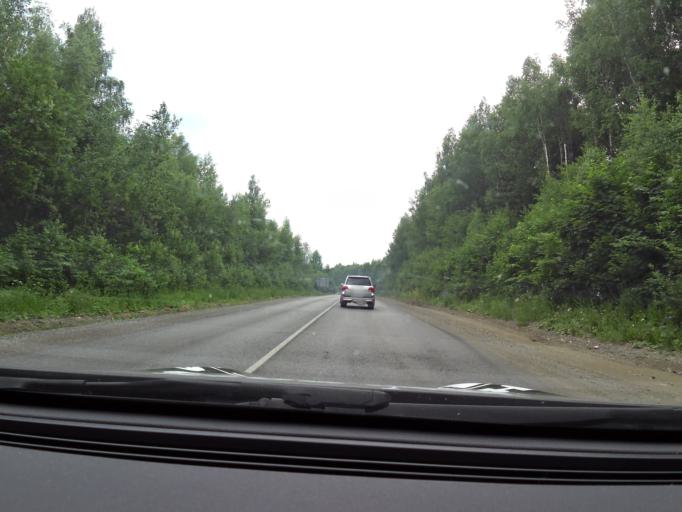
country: RU
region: Chelyabinsk
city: Sim
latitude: 54.9982
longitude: 57.6098
